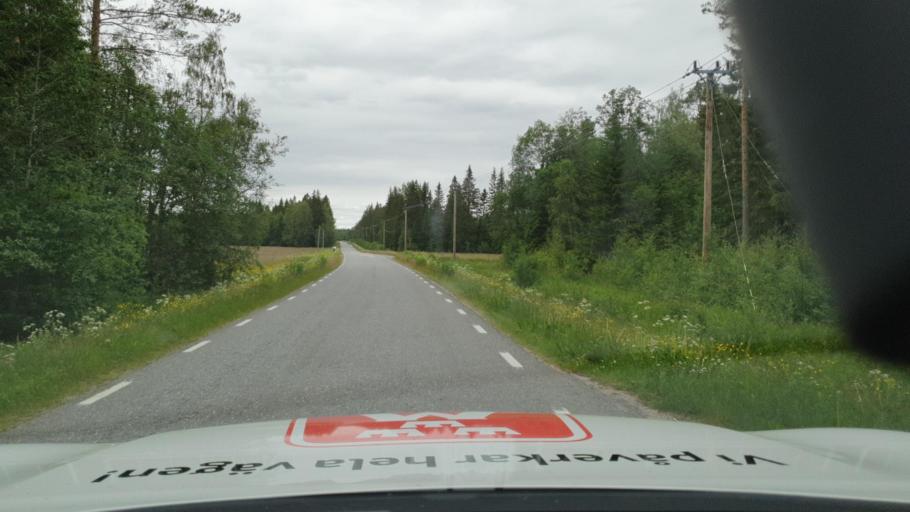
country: SE
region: Vaesterbotten
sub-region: Nordmalings Kommun
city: Nordmaling
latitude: 63.5193
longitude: 19.4209
